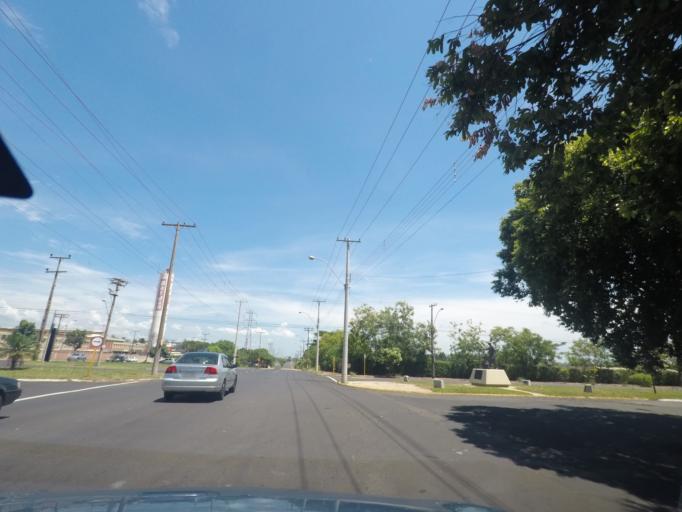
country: BR
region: Sao Paulo
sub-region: Matao
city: Matao
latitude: -21.6134
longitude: -48.3704
